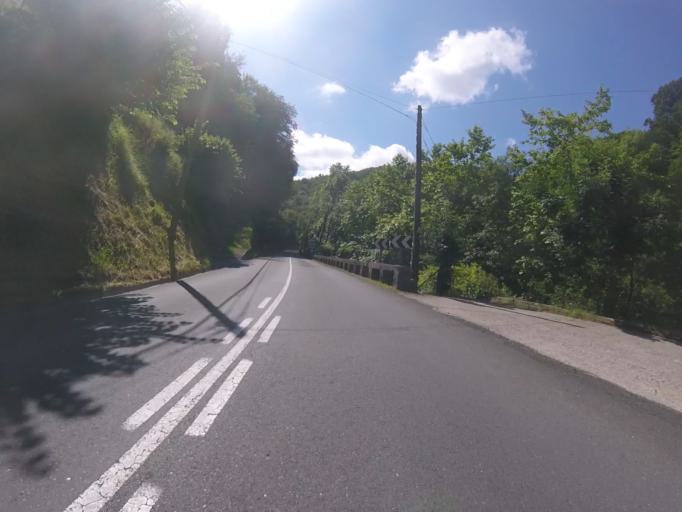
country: ES
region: Basque Country
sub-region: Provincia de Guipuzcoa
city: Azpeitia
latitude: 43.1749
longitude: -2.2222
